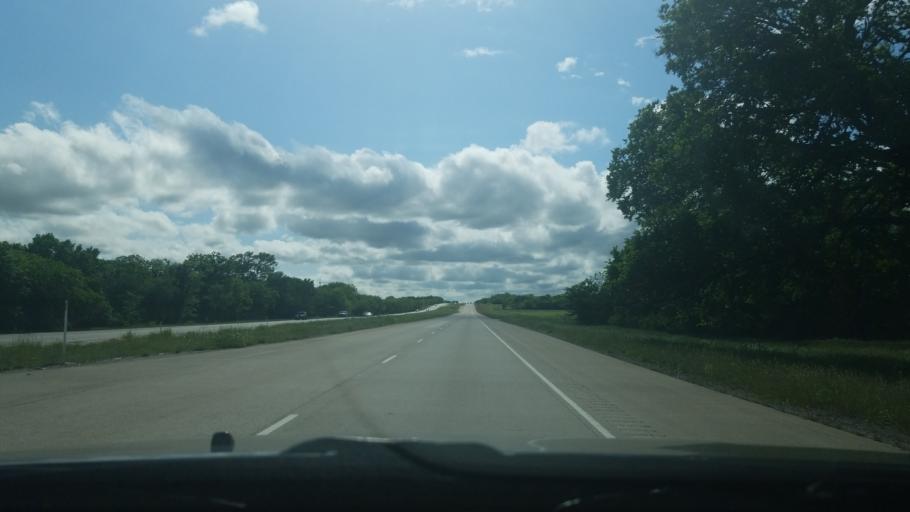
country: US
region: Texas
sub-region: Wise County
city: Decatur
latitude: 33.2459
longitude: -97.4518
